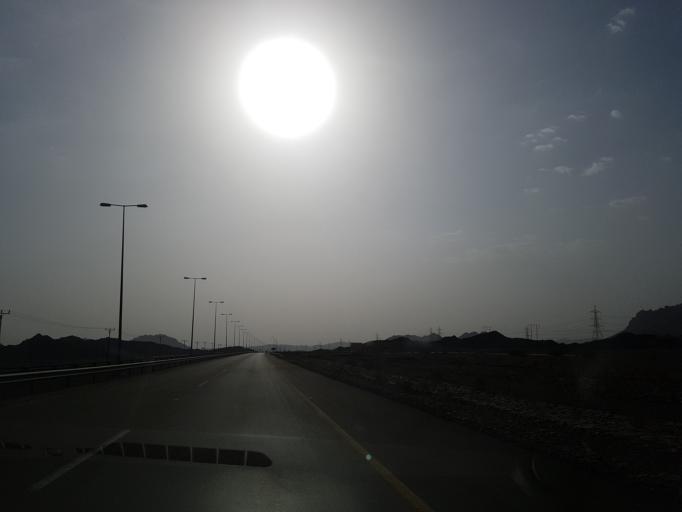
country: OM
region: Al Buraimi
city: Al Buraymi
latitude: 24.2471
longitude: 56.0275
